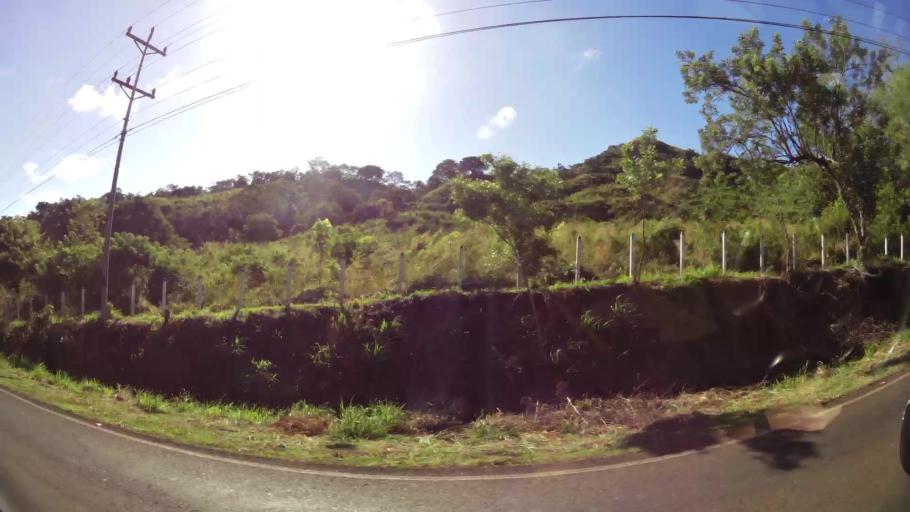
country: CR
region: Guanacaste
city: Belen
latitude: 10.3698
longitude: -85.6387
